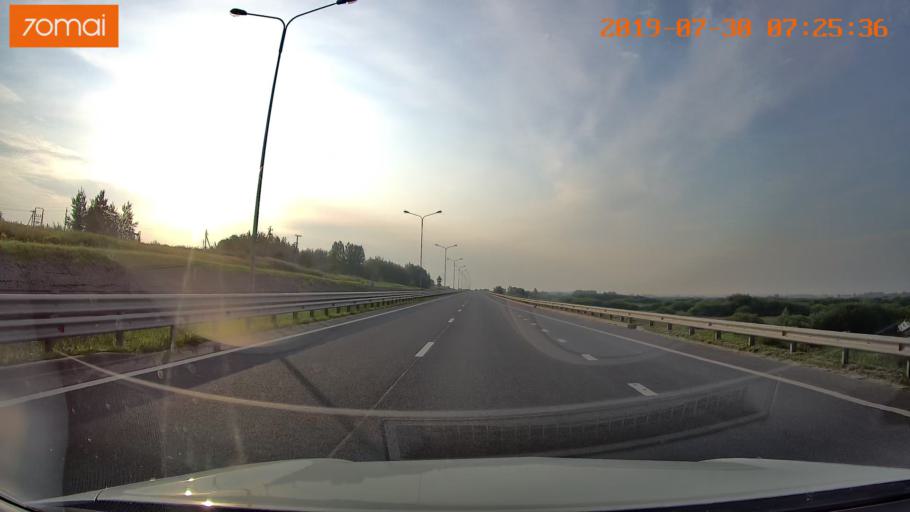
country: RU
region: Kaliningrad
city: Gvardeysk
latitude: 54.6860
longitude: 20.8381
